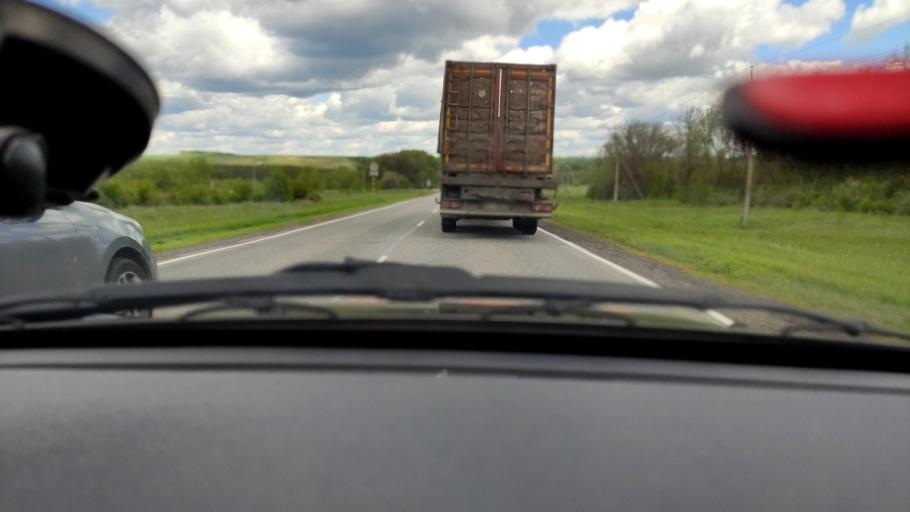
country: RU
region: Voronezj
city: Uryv-Pokrovka
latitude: 51.1234
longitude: 39.0372
